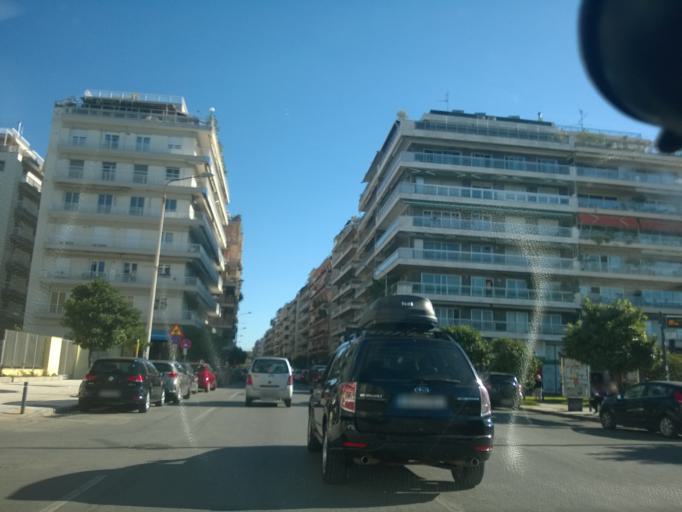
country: GR
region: Central Macedonia
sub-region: Nomos Thessalonikis
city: Kalamaria
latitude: 40.6017
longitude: 22.9508
